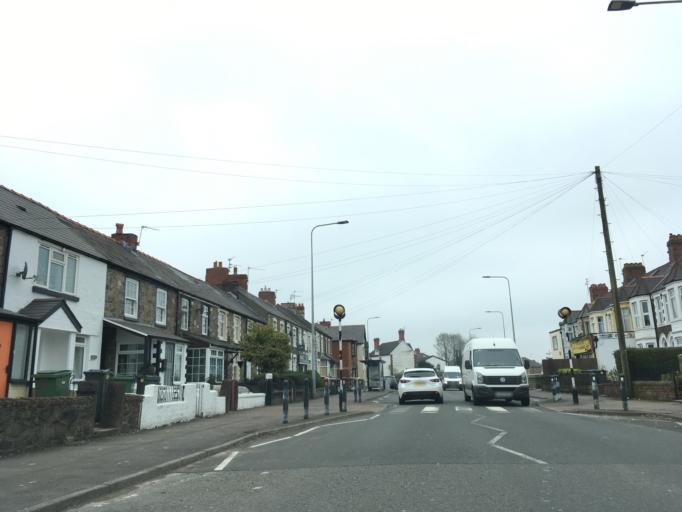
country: GB
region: Wales
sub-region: Cardiff
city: Cardiff
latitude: 51.5095
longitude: -3.2063
